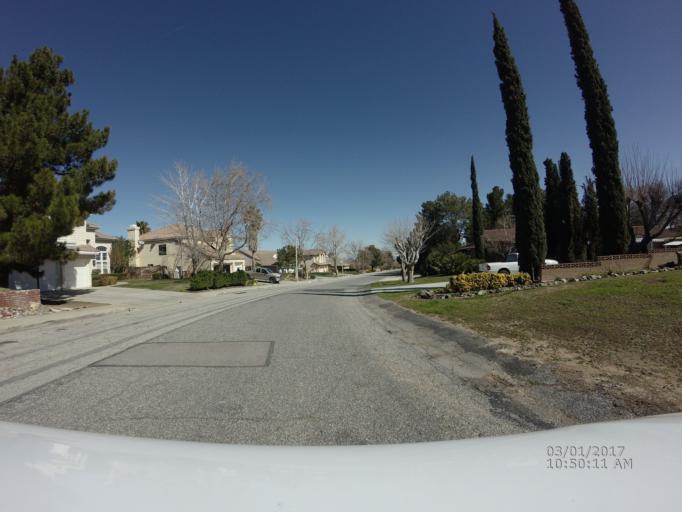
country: US
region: California
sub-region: Los Angeles County
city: Leona Valley
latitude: 34.6465
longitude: -118.2592
